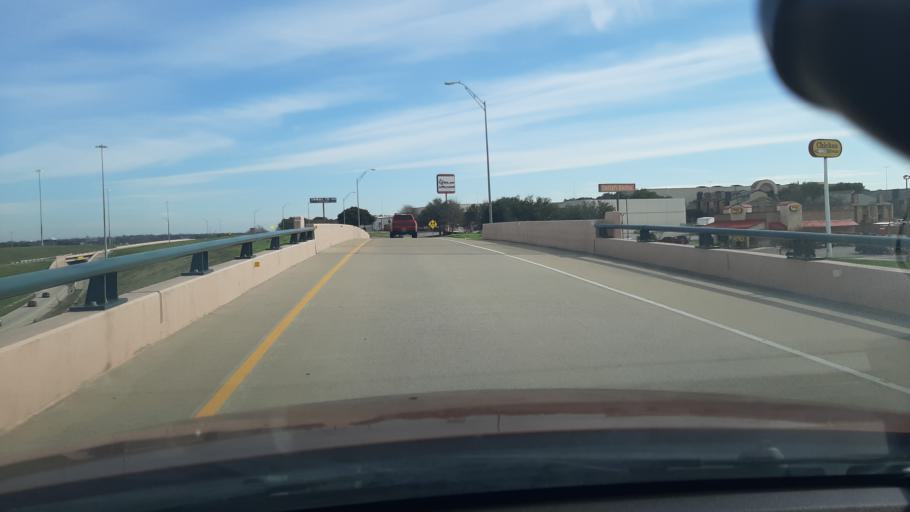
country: US
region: Texas
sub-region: Tarrant County
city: Benbrook
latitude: 32.6821
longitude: -97.4027
